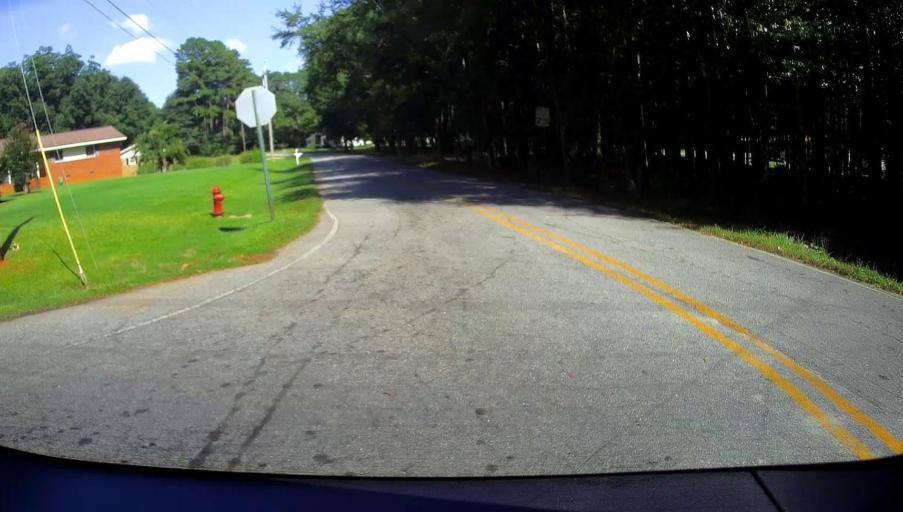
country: US
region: Georgia
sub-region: Upson County
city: Hannahs Mill
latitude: 32.9439
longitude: -84.3443
